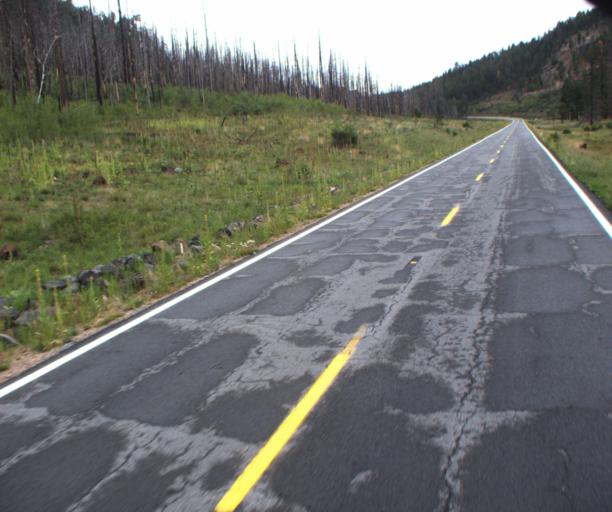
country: US
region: Arizona
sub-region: Apache County
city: Eagar
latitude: 33.7996
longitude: -109.1544
